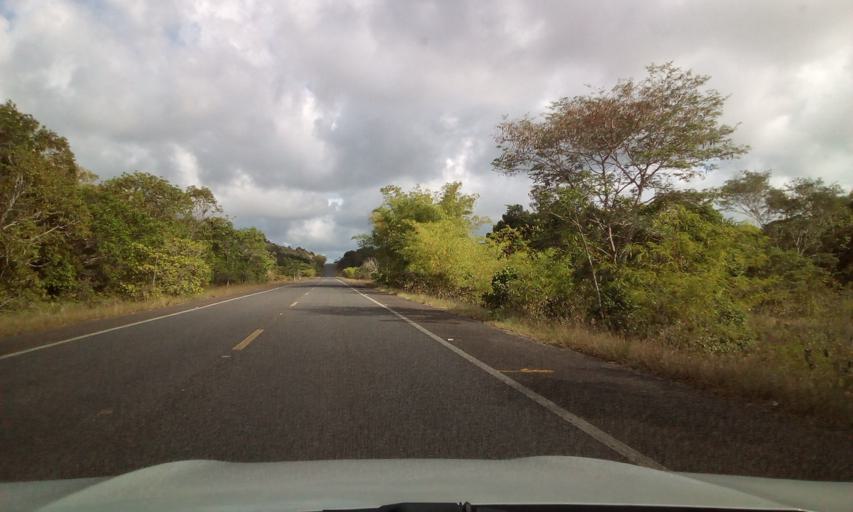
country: BR
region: Sergipe
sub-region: Indiaroba
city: Indiaroba
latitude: -11.5963
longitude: -37.5419
